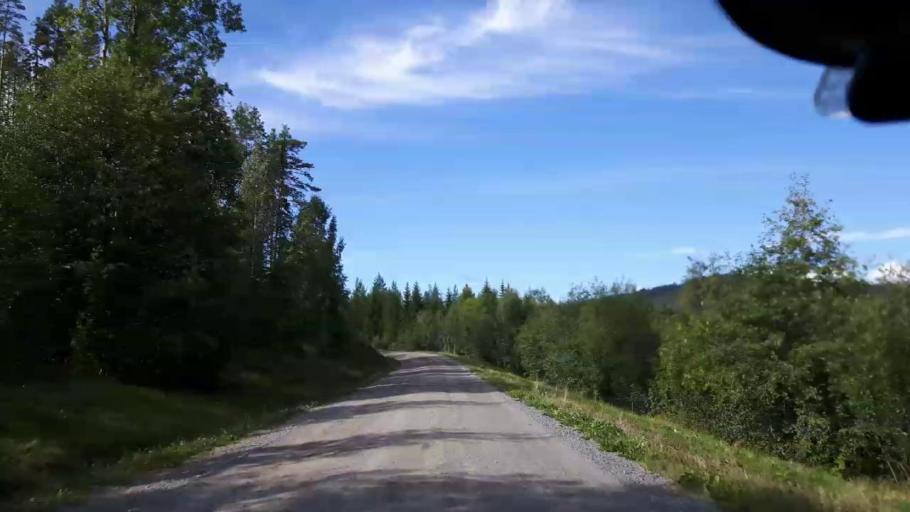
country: SE
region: Jaemtland
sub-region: Ragunda Kommun
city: Hammarstrand
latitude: 63.1355
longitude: 16.1101
